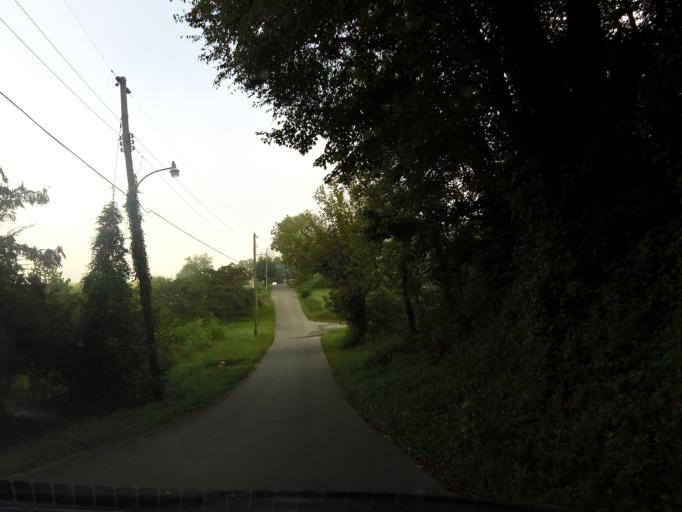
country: US
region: Tennessee
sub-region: Campbell County
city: Jellico
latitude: 36.5809
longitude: -84.1319
